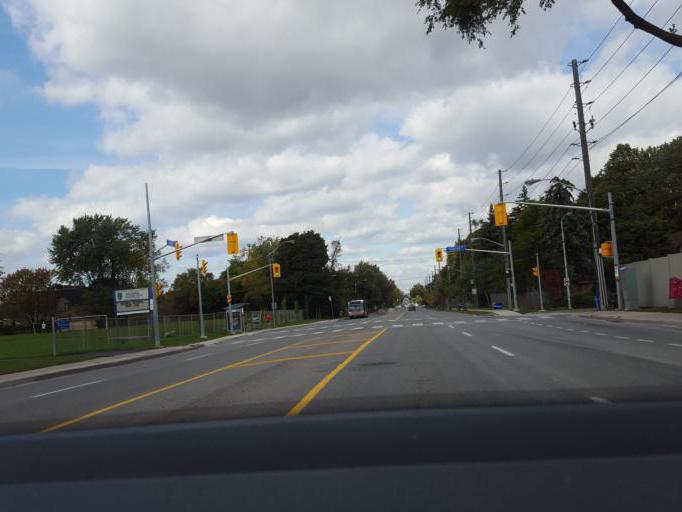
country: CA
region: Ontario
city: Willowdale
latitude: 43.7406
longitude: -79.3572
